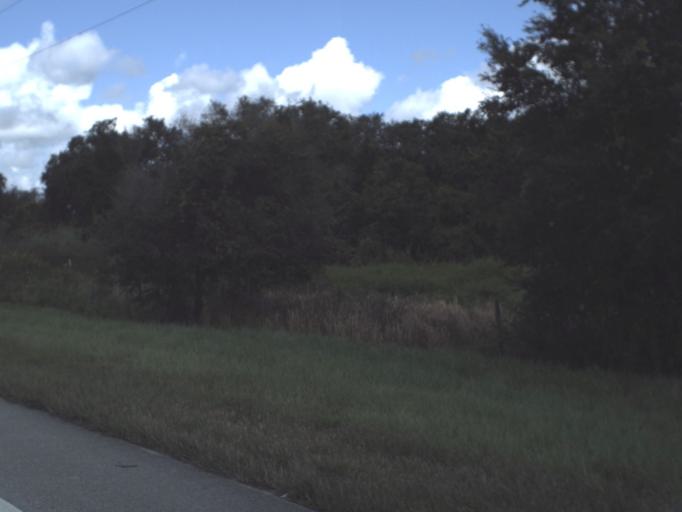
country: US
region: Florida
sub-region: Highlands County
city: Lake Placid
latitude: 27.3888
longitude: -81.1416
